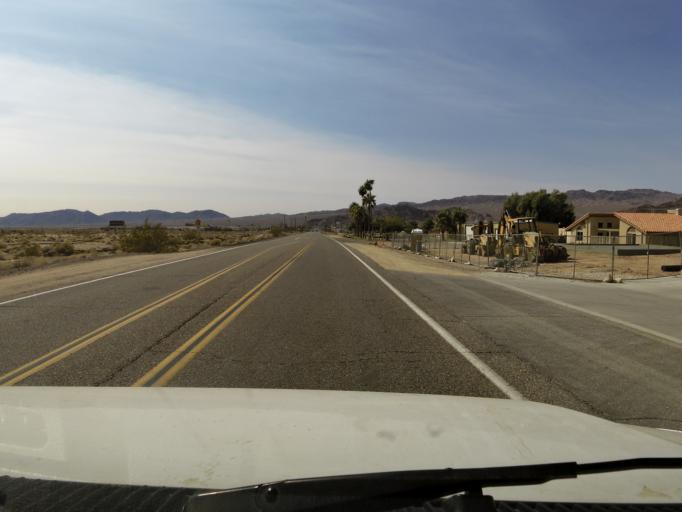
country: US
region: California
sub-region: San Bernardino County
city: Fort Irwin
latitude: 35.2740
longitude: -116.0614
